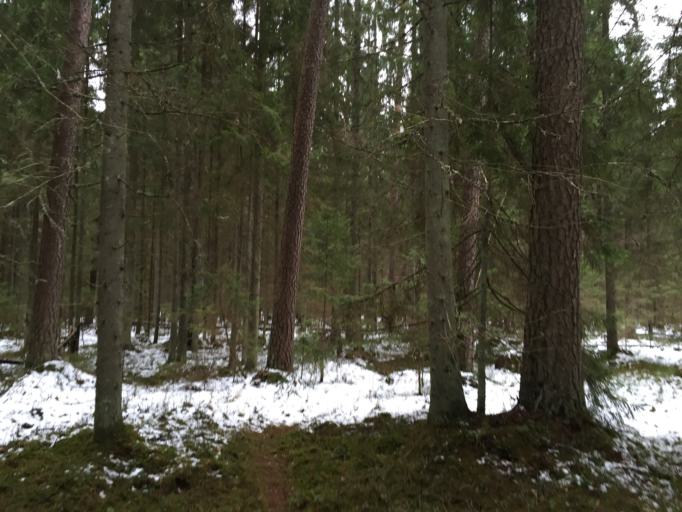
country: LV
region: Garkalne
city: Garkalne
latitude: 56.9656
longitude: 24.4725
